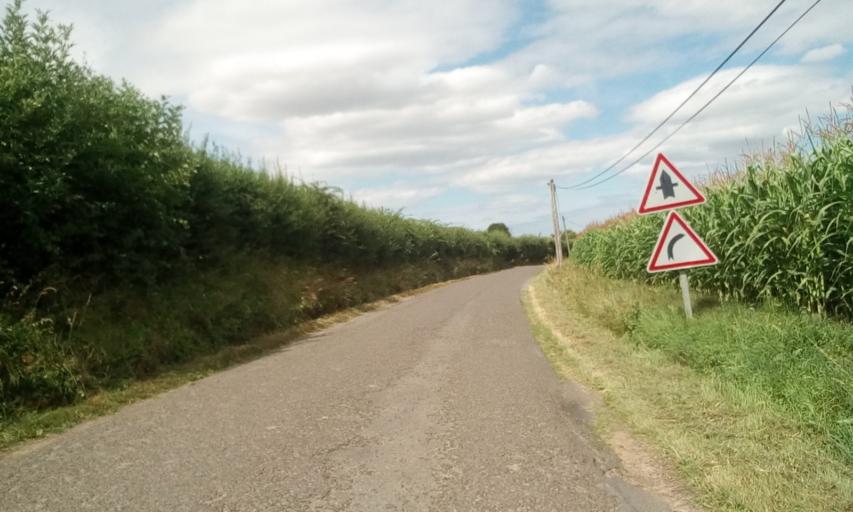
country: FR
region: Lower Normandy
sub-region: Departement du Calvados
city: Sannerville
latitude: 49.1657
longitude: -0.2136
